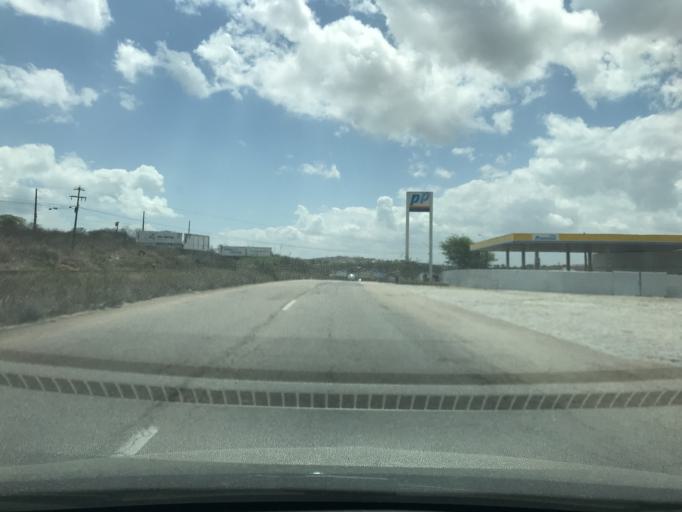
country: BR
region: Pernambuco
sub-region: Caruaru
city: Caruaru
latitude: -8.3087
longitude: -35.9491
